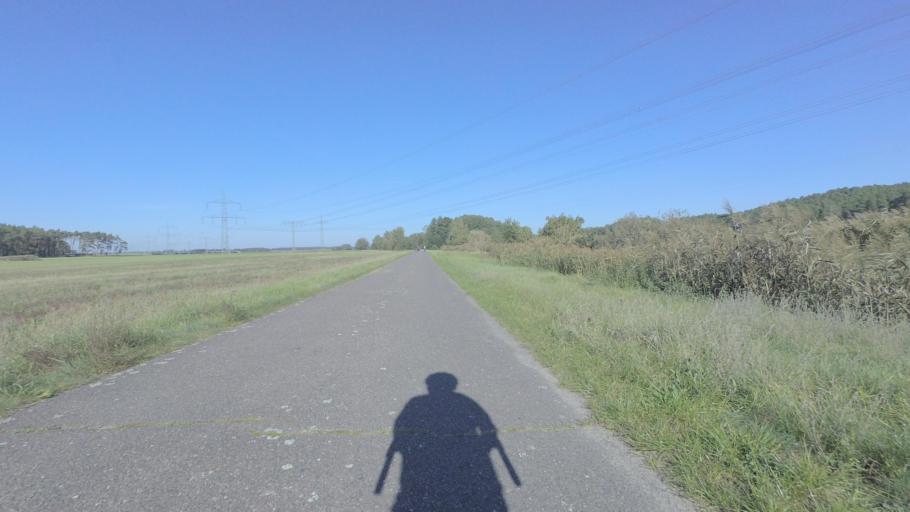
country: DE
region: Brandenburg
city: Am Mellensee
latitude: 52.2014
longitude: 13.3374
